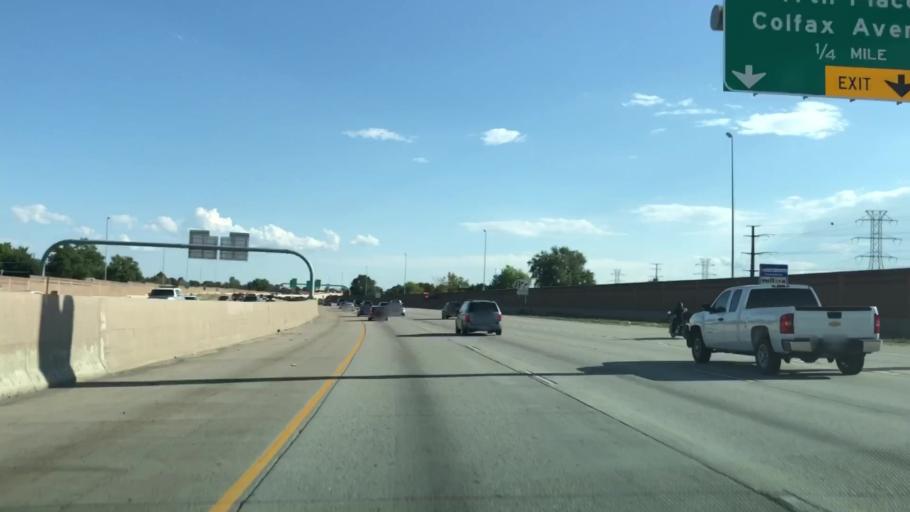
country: US
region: Colorado
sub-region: Adams County
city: Aurora
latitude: 39.7537
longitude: -104.8279
